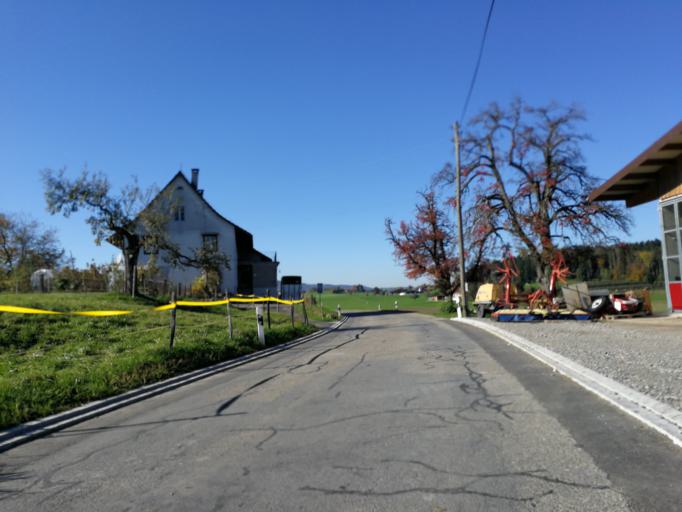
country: CH
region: Zurich
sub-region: Bezirk Hinwil
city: Binzikon
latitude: 47.2643
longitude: 8.7579
